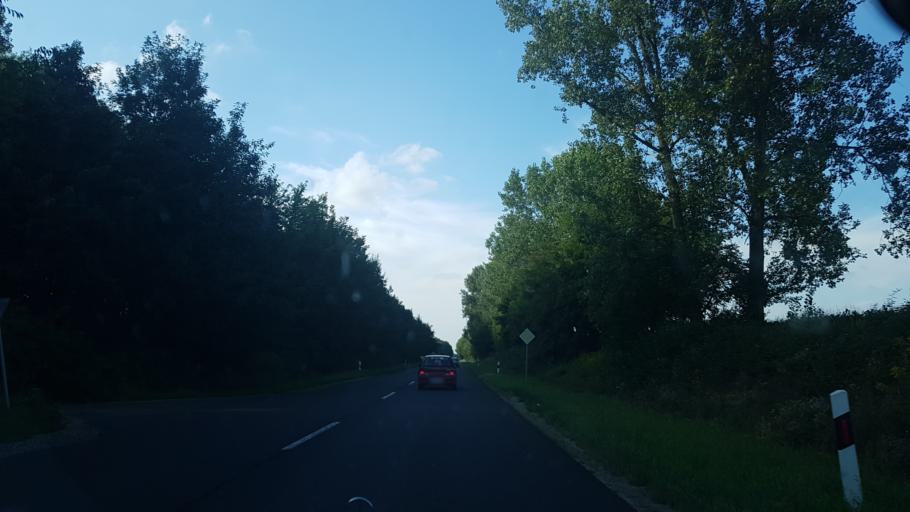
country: HU
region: Somogy
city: Segesd
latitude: 46.3143
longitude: 17.3483
